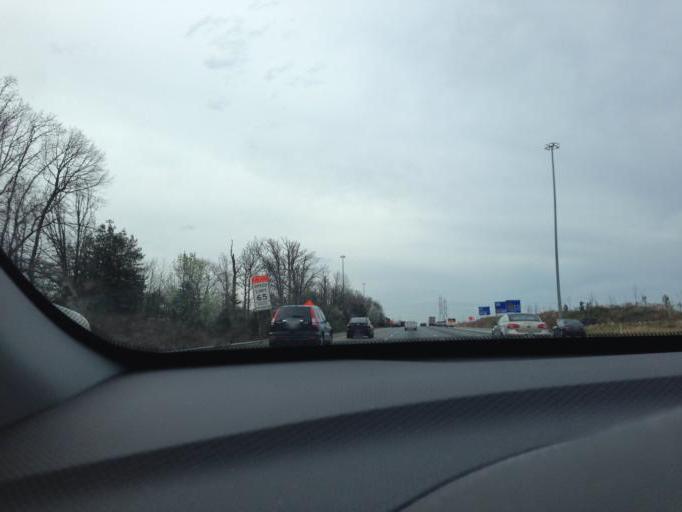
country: US
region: Maryland
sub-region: Prince George's County
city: West Laurel
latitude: 39.0779
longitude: -76.9023
